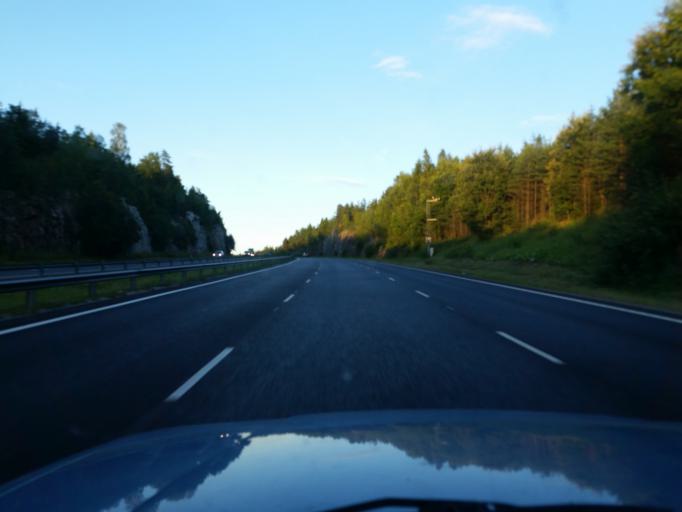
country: FI
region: Varsinais-Suomi
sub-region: Turku
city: Paimio
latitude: 60.4236
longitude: 22.6810
